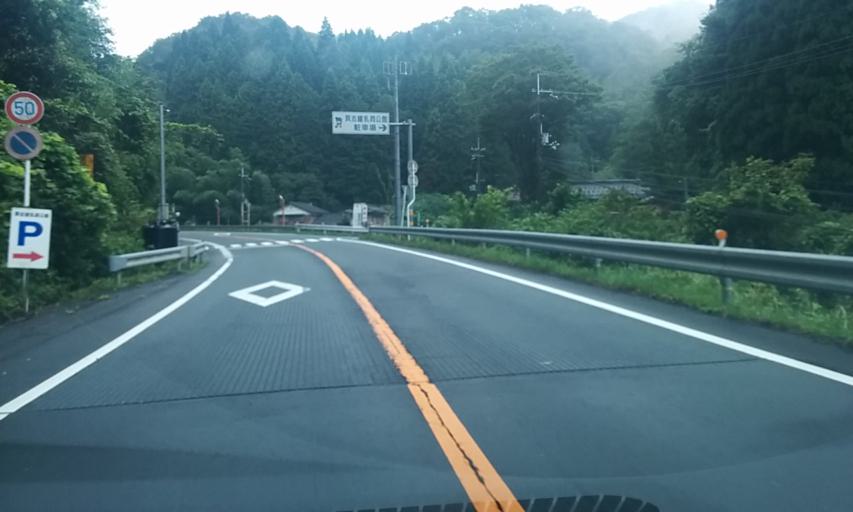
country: JP
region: Kyoto
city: Ayabe
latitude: 35.2377
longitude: 135.3242
